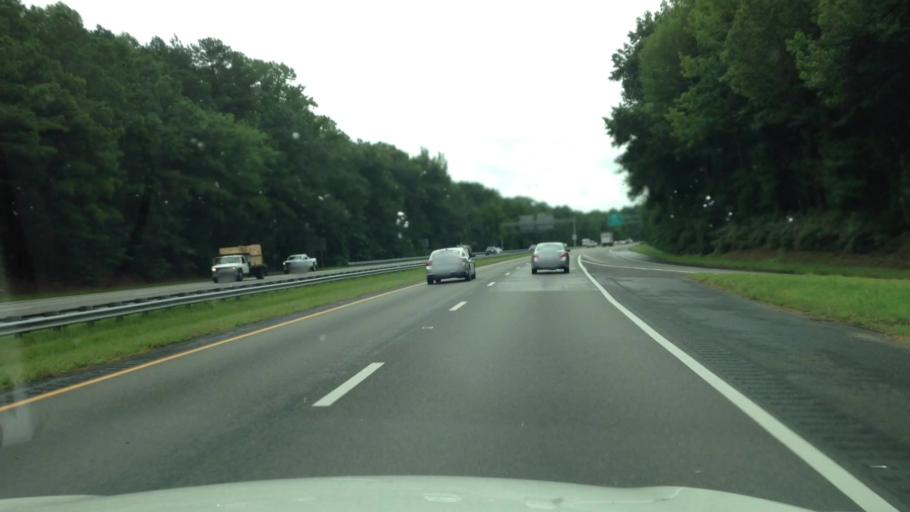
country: US
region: Virginia
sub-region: City of Petersburg
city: Petersburg
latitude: 37.2122
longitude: -77.3749
